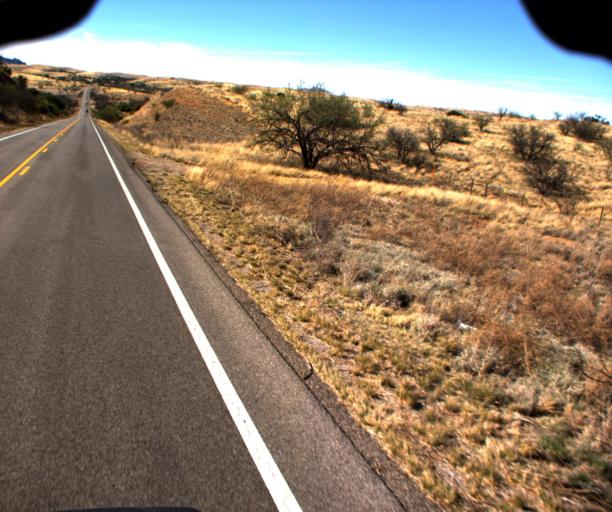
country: US
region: Arizona
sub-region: Pima County
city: Corona de Tucson
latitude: 31.7759
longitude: -110.6882
